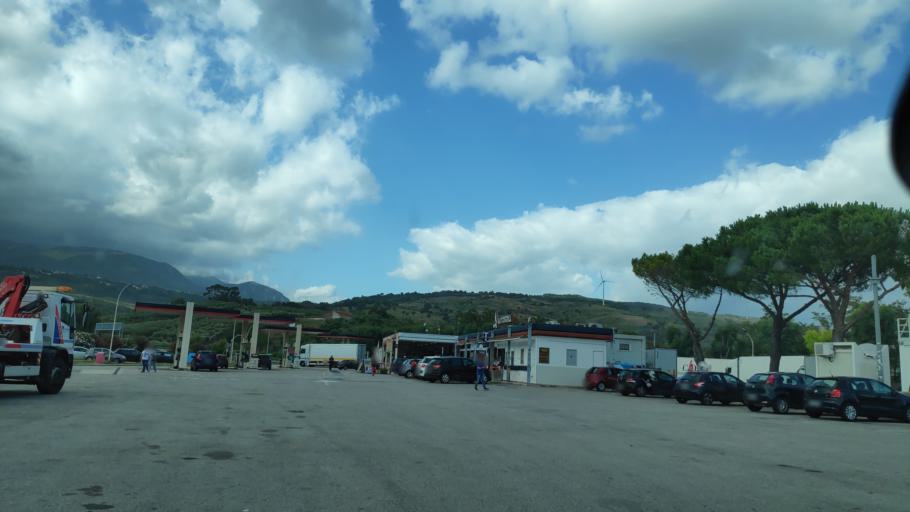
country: IT
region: Campania
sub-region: Provincia di Salerno
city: Serre
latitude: 40.6235
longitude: 15.1825
